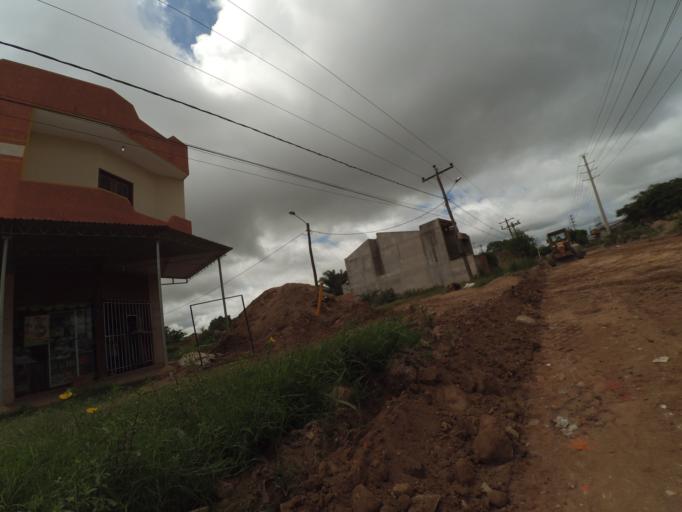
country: BO
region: Santa Cruz
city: Santa Cruz de la Sierra
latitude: -17.8636
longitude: -63.2277
